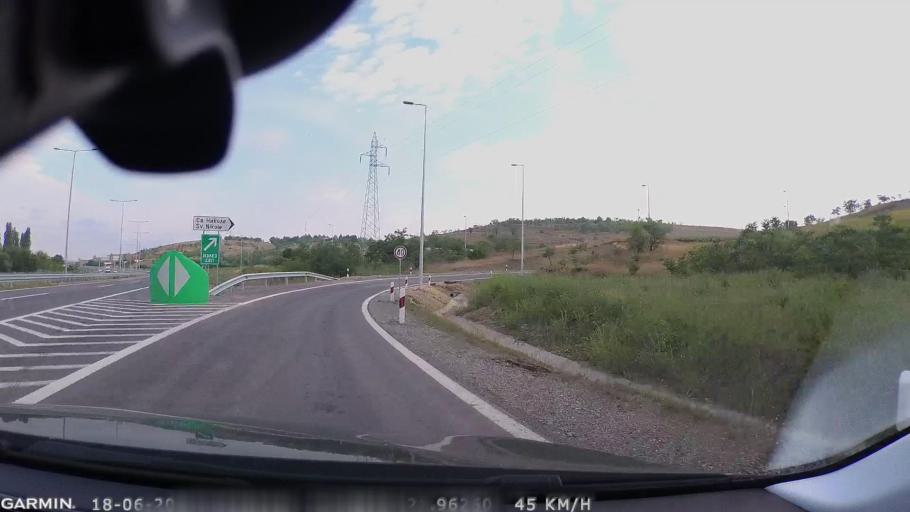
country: MK
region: Sveti Nikole
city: Sveti Nikole
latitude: 41.8562
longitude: 21.9627
